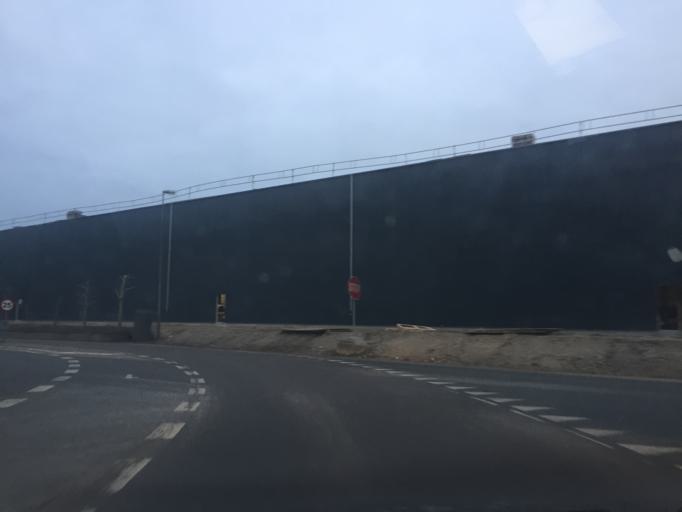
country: DK
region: Zealand
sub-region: Koge Kommune
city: Koge
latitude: 55.4643
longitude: 12.1915
